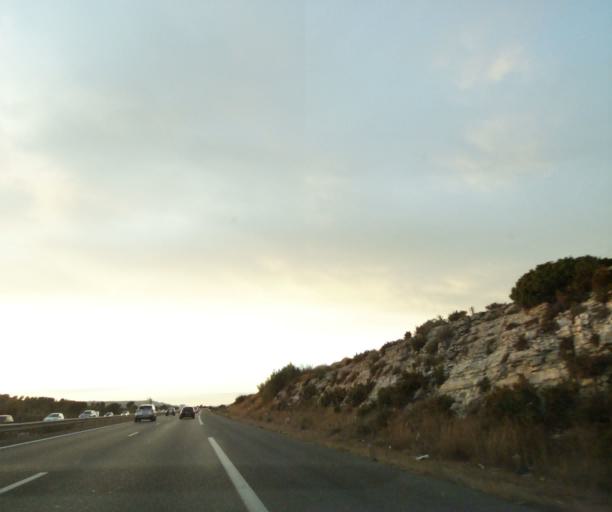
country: FR
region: Provence-Alpes-Cote d'Azur
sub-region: Departement des Bouches-du-Rhone
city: Gignac-la-Nerthe
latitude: 43.3803
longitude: 5.2177
